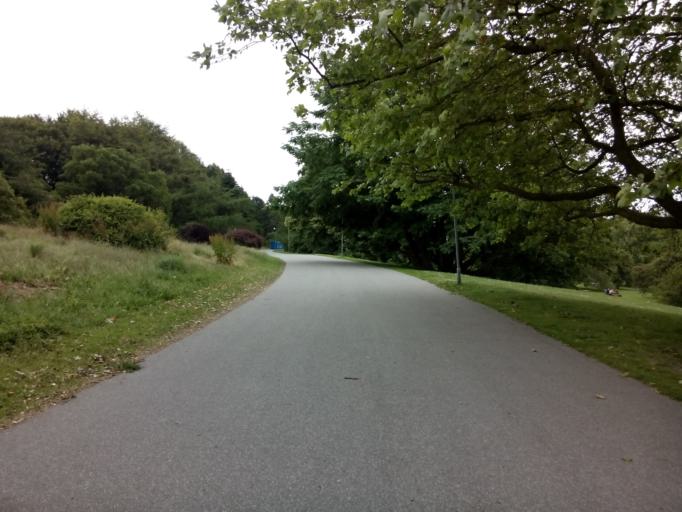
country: DK
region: Central Jutland
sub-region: Arhus Kommune
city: Arhus
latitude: 56.1638
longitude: 10.1880
